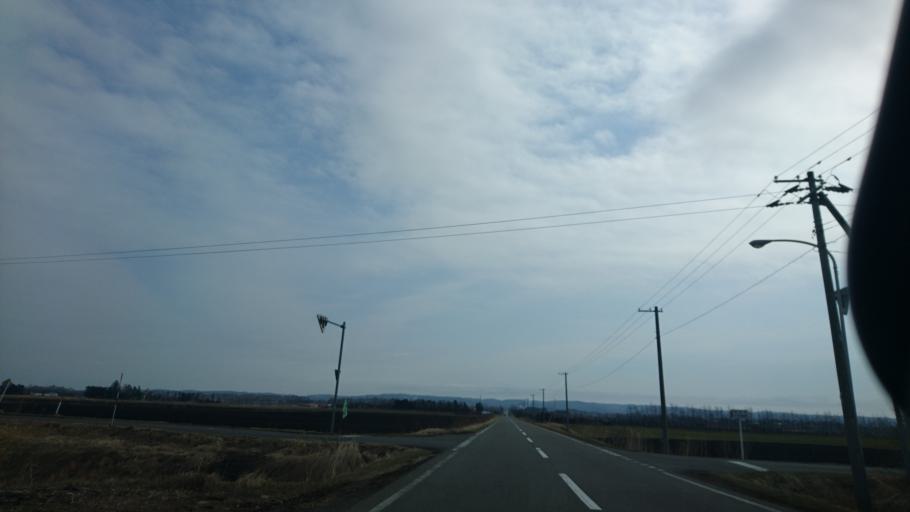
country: JP
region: Hokkaido
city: Otofuke
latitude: 43.0396
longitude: 143.2305
